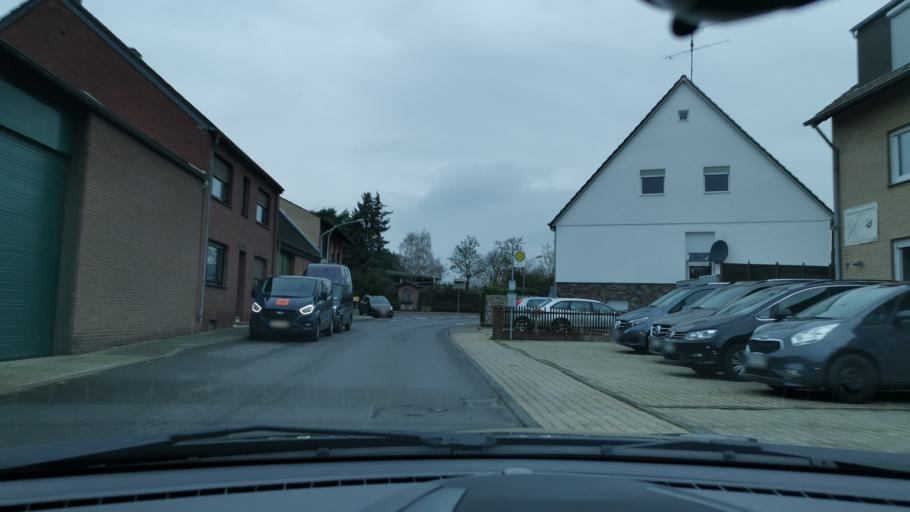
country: DE
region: North Rhine-Westphalia
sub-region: Regierungsbezirk Dusseldorf
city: Neubrueck
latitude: 51.1335
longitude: 6.6391
